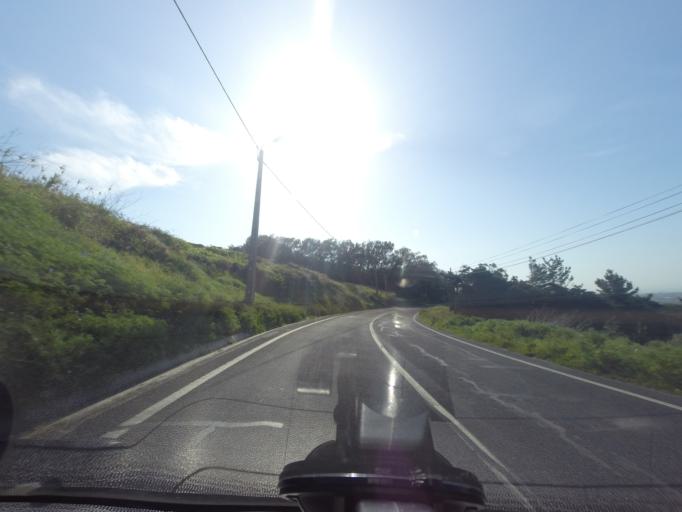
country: PT
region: Lisbon
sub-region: Sintra
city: Colares
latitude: 38.7585
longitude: -9.4632
